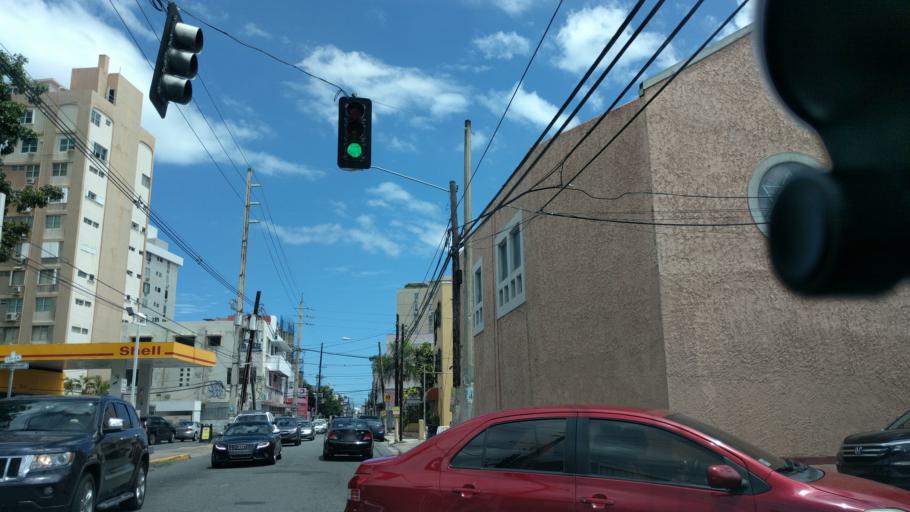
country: PR
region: San Juan
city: San Juan
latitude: 18.4518
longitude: -66.0617
